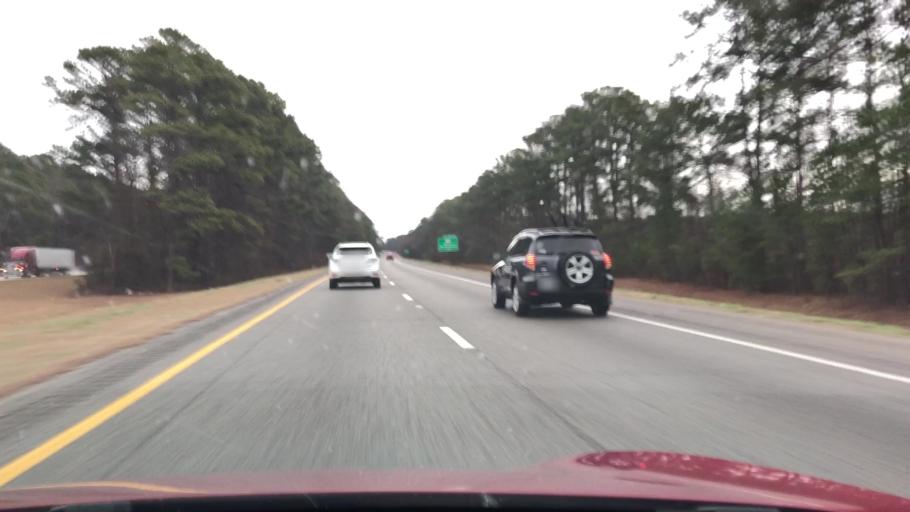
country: US
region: South Carolina
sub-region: Dillon County
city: Latta
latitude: 34.3345
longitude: -79.5552
